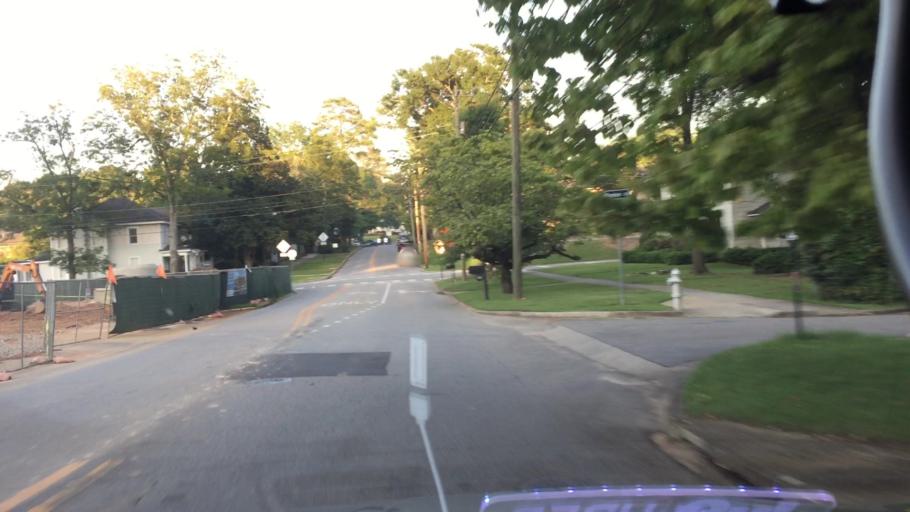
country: US
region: Alabama
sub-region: Lee County
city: Auburn
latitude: 32.6065
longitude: -85.4758
